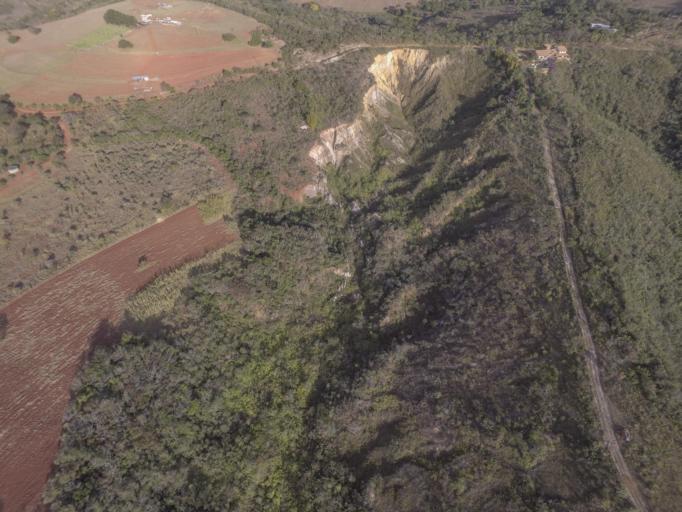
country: BR
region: Minas Gerais
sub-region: Tiradentes
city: Tiradentes
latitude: -21.0561
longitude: -44.1037
